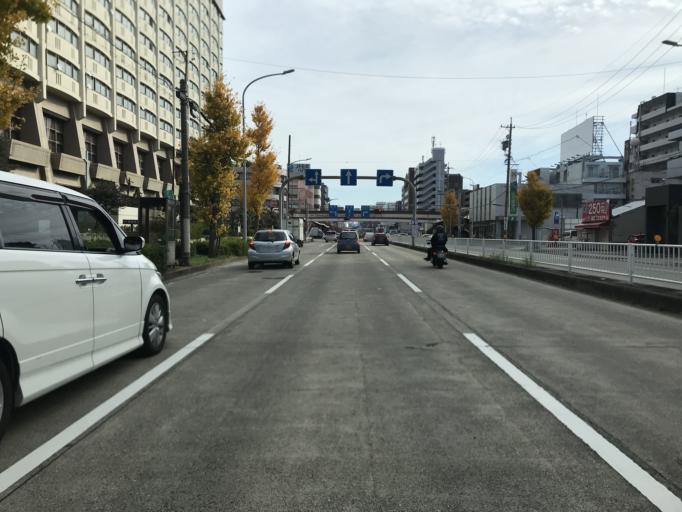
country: JP
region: Aichi
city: Nagoya-shi
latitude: 35.1883
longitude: 136.8743
